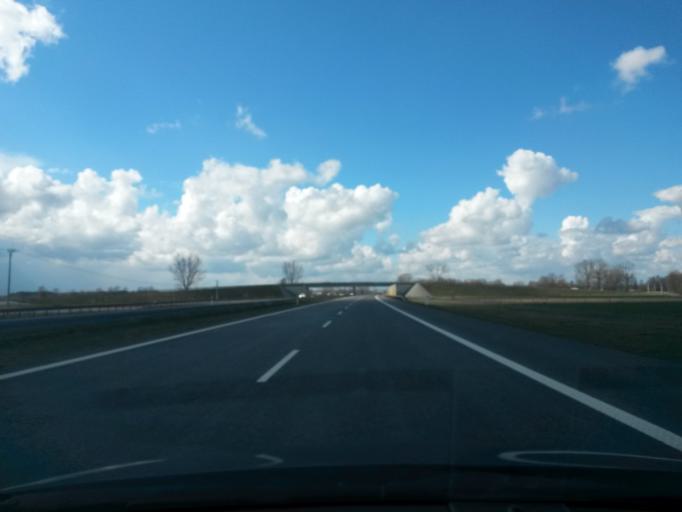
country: PL
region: Lodz Voivodeship
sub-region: Powiat poddebicki
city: Wartkowice
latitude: 52.0035
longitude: 18.9913
